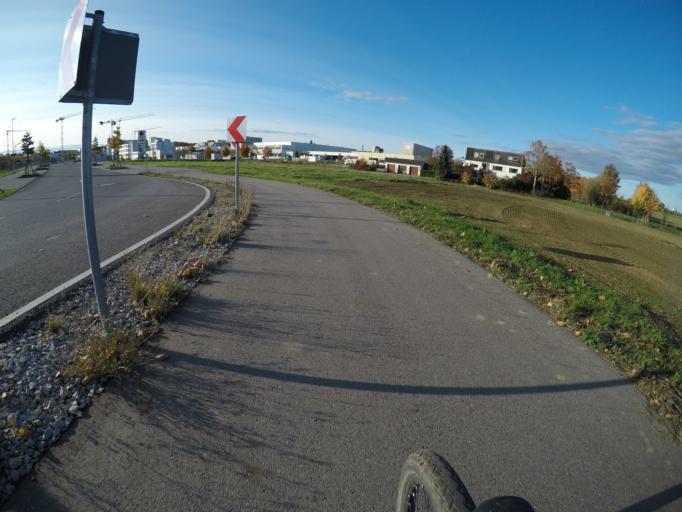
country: DE
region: Baden-Wuerttemberg
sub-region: Regierungsbezirk Stuttgart
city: Leinfelden-Echterdingen
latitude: 48.6944
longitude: 9.1504
